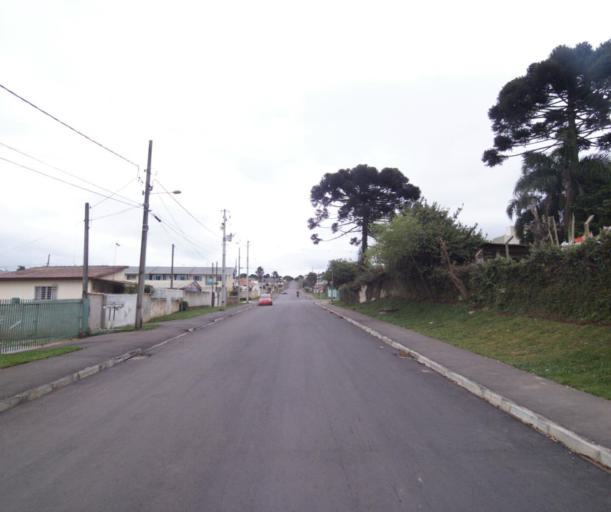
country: BR
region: Parana
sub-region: Quatro Barras
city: Quatro Barras
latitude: -25.3637
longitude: -49.1089
